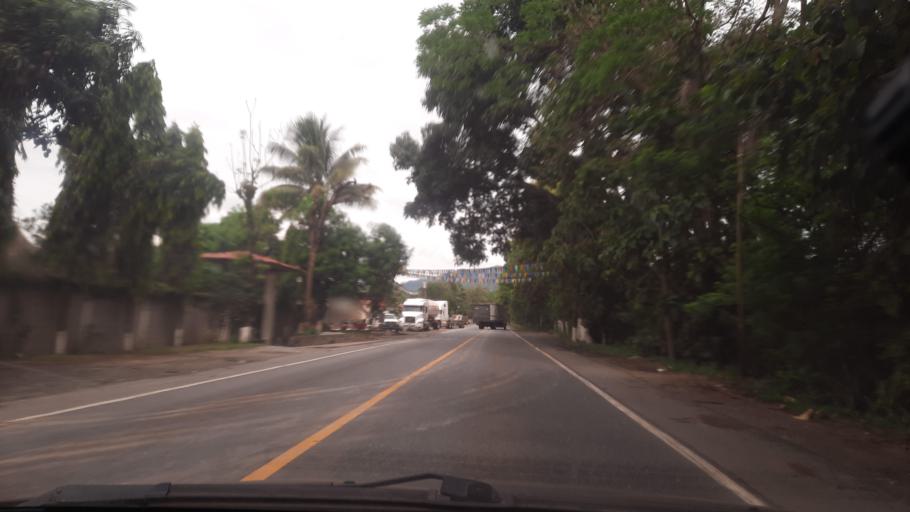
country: GT
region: Izabal
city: Morales
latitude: 15.4641
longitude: -88.9135
